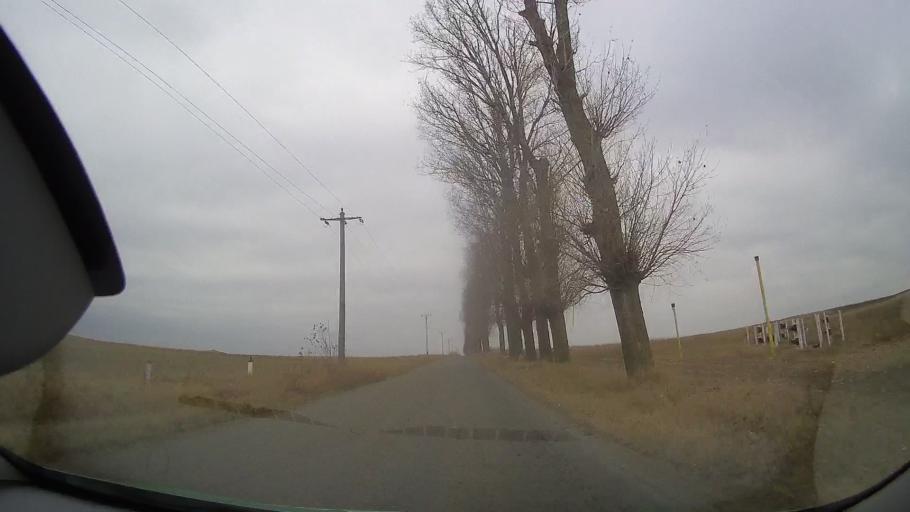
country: RO
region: Buzau
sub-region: Comuna Pogoanele
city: Pogoanele
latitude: 44.9630
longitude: 27.0217
